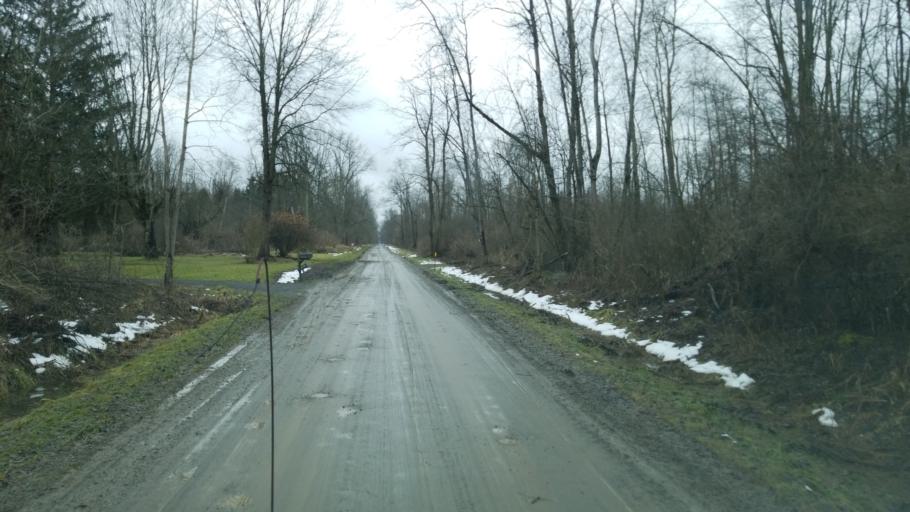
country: US
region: Ohio
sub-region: Ashtabula County
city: Orwell
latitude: 41.4439
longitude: -80.9349
